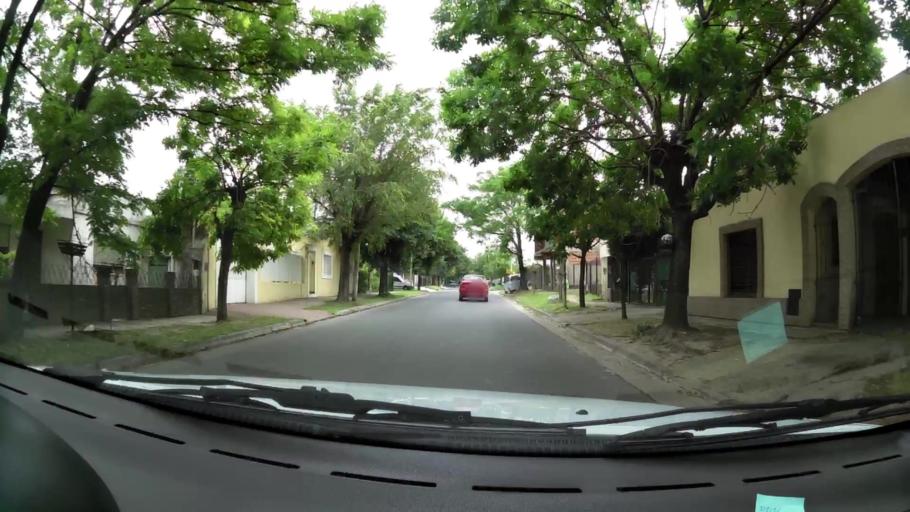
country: AR
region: Buenos Aires
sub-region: Partido de Ezeiza
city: Ezeiza
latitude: -34.8445
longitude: -58.5131
